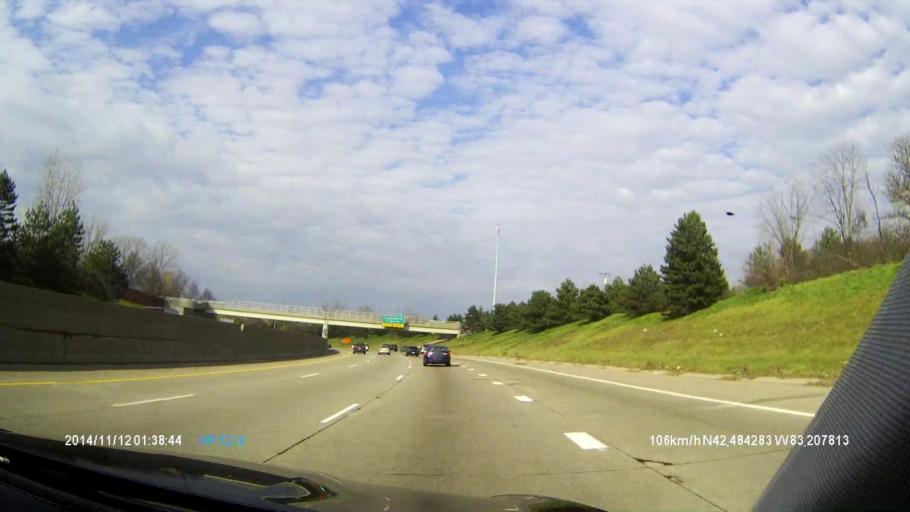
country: US
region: Michigan
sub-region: Oakland County
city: Southfield
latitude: 42.4844
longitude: -83.2079
